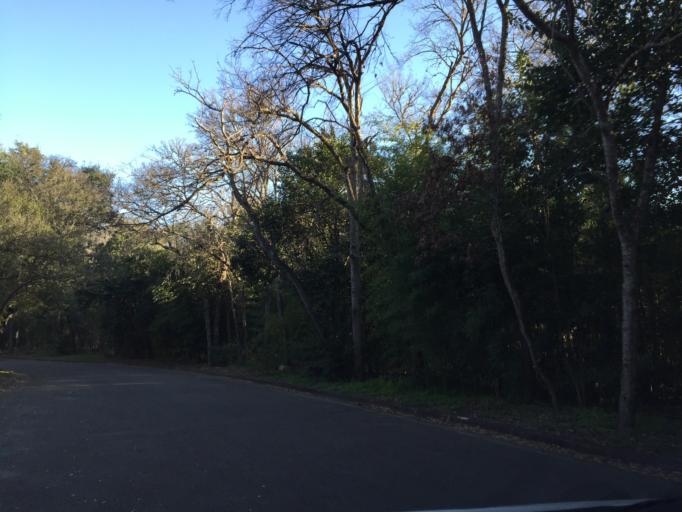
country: US
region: Texas
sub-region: Travis County
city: Rollingwood
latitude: 30.2104
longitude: -97.7997
